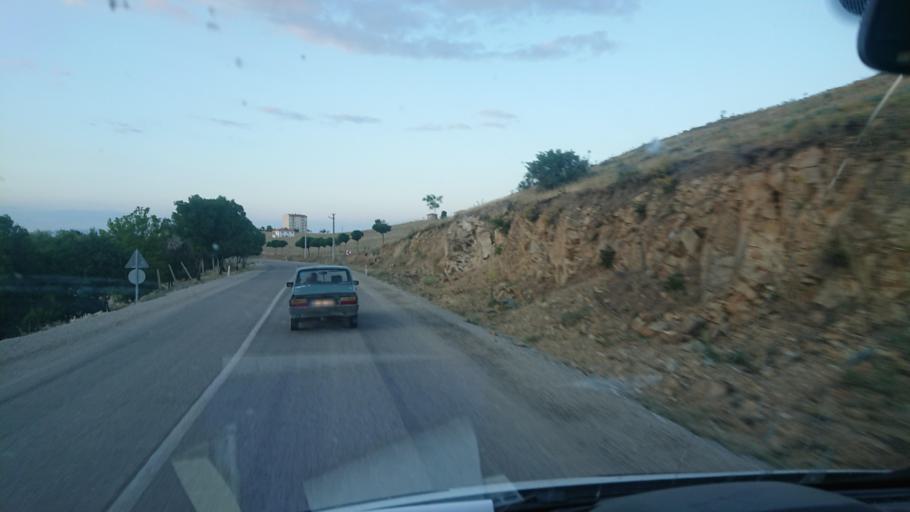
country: TR
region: Aksaray
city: Sariyahsi
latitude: 38.9682
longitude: 33.8273
